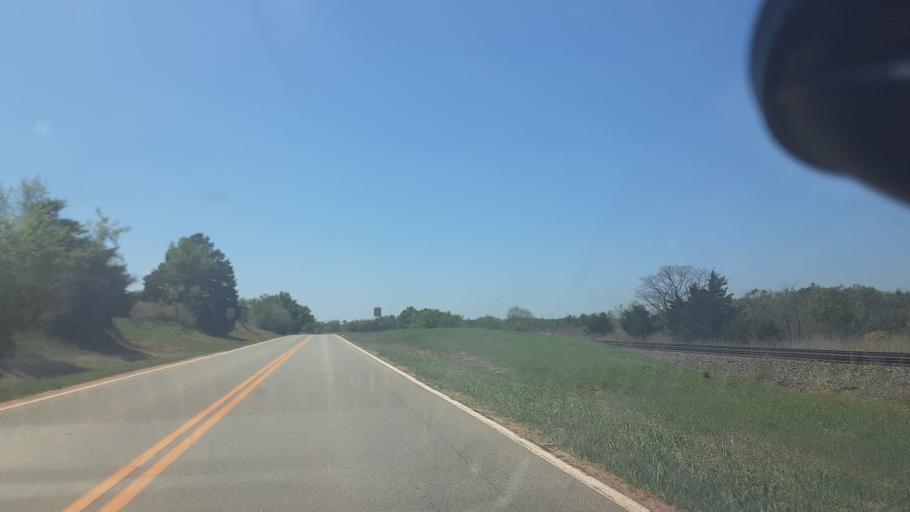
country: US
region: Oklahoma
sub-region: Logan County
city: Langston
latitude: 36.0774
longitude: -97.4027
